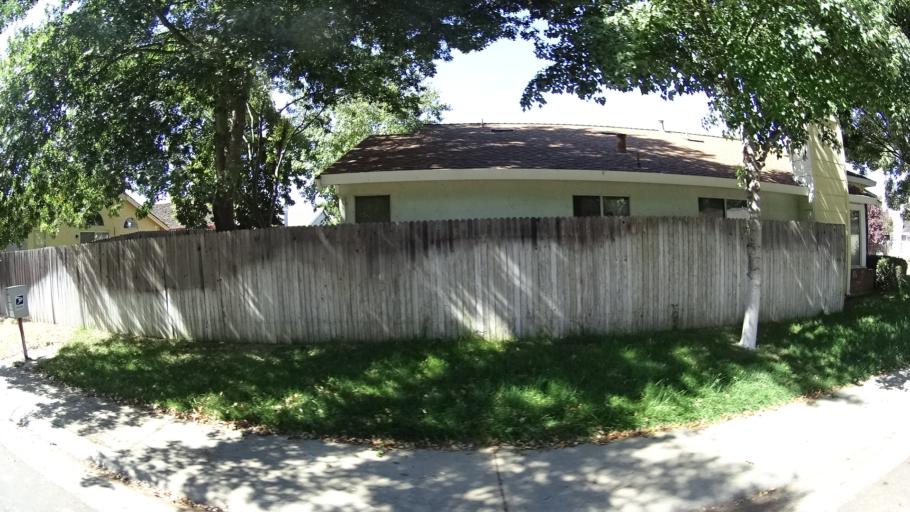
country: US
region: California
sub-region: Sacramento County
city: Laguna
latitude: 38.4262
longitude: -121.4275
